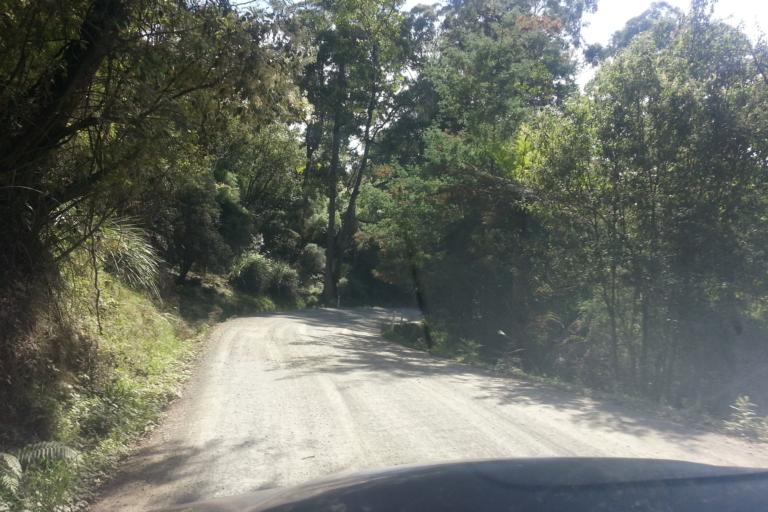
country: AU
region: Victoria
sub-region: Cardinia
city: Cockatoo
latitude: -37.9786
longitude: 145.4809
